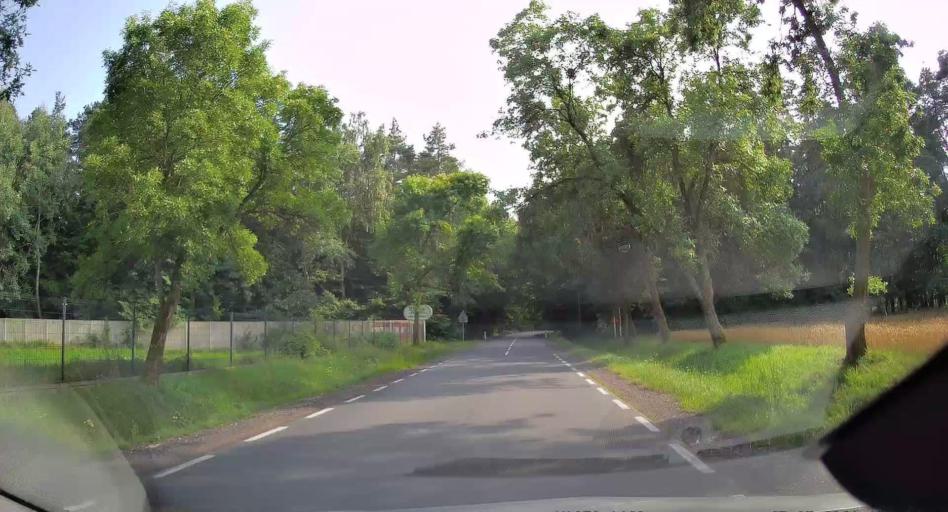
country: PL
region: Lodz Voivodeship
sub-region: Powiat tomaszowski
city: Rzeczyca
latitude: 51.5775
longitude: 20.2827
